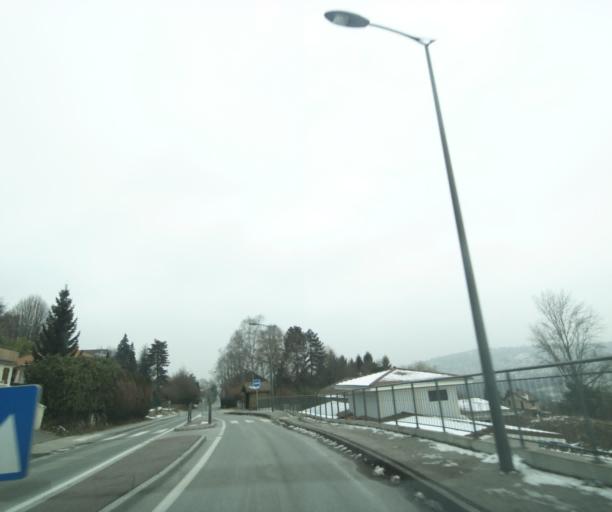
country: FR
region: Rhone-Alpes
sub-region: Departement de la Haute-Savoie
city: Vetraz-Monthoux
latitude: 46.1672
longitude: 6.2386
